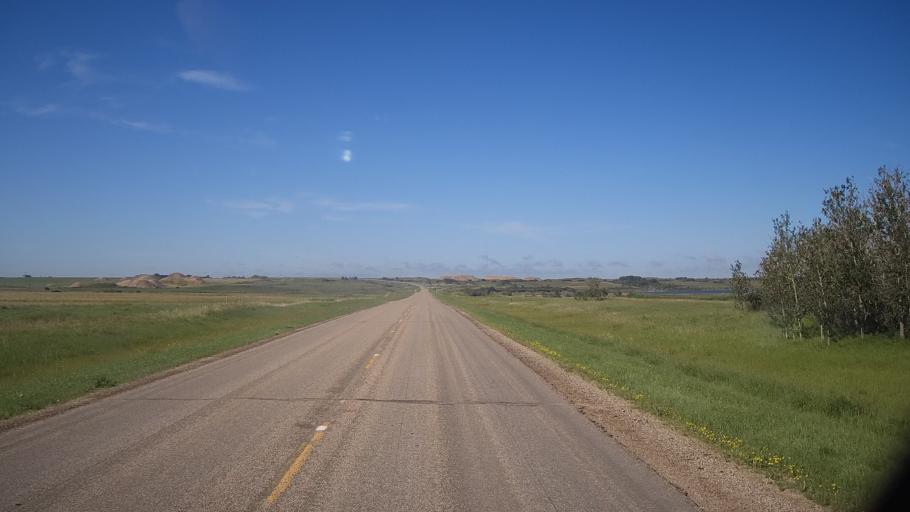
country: CA
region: Saskatchewan
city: Watrous
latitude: 51.7158
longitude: -105.3658
